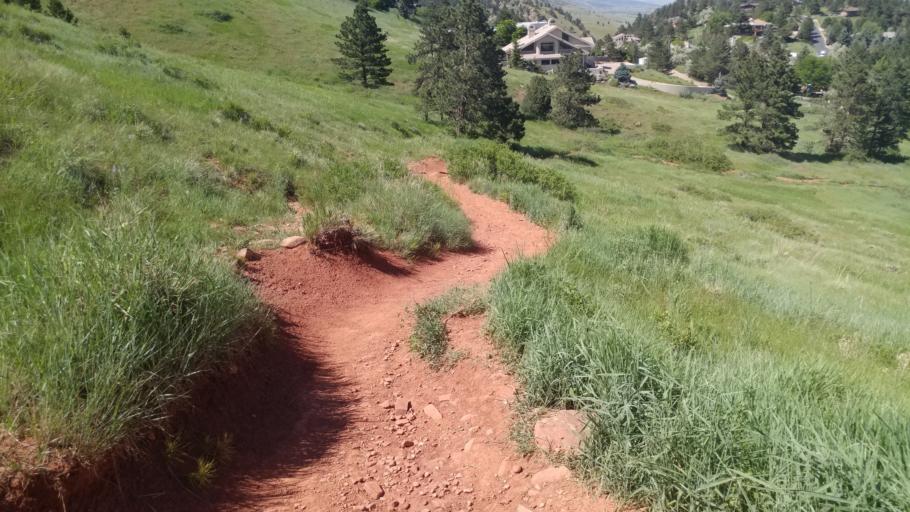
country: US
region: Colorado
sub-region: Boulder County
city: Boulder
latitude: 40.0350
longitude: -105.3001
